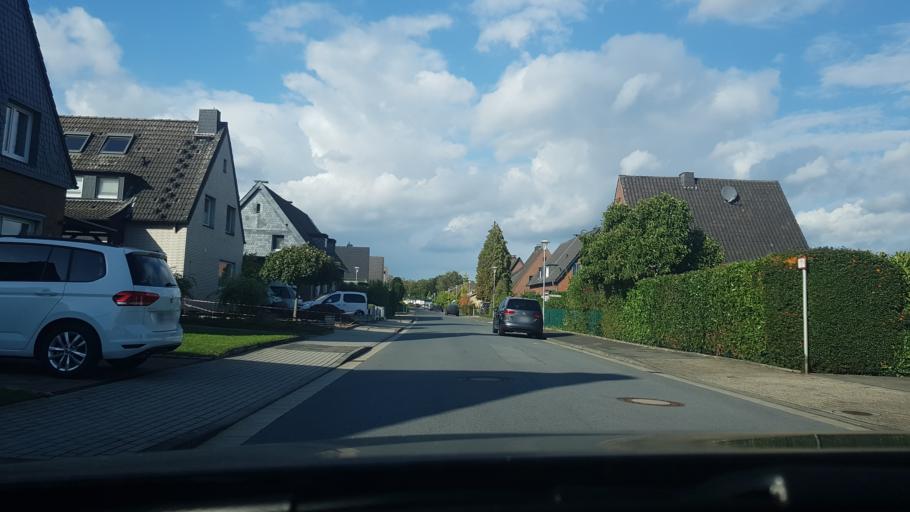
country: DE
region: North Rhine-Westphalia
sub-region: Regierungsbezirk Dusseldorf
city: Moers
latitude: 51.4210
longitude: 6.5908
